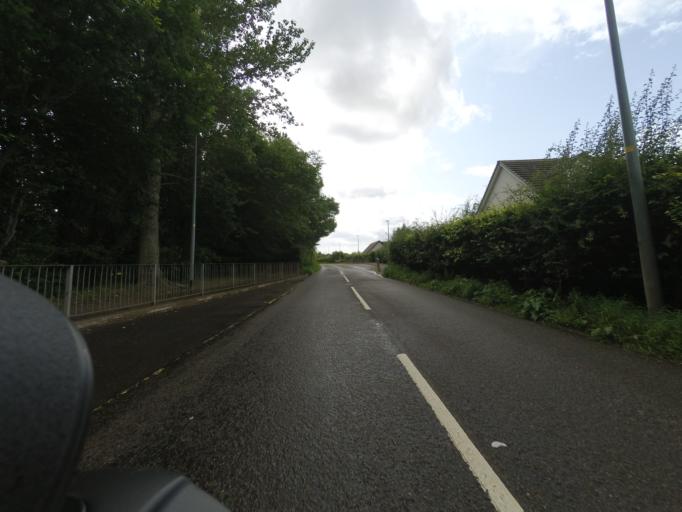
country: GB
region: Scotland
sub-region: Highland
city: Tain
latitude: 57.7418
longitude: -4.0775
